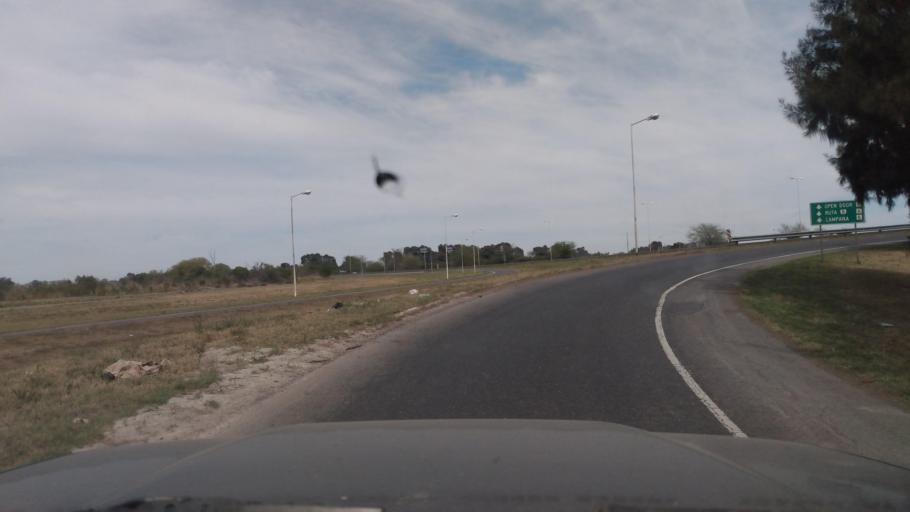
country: AR
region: Buenos Aires
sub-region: Partido de Lujan
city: Lujan
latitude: -34.5749
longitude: -59.0360
